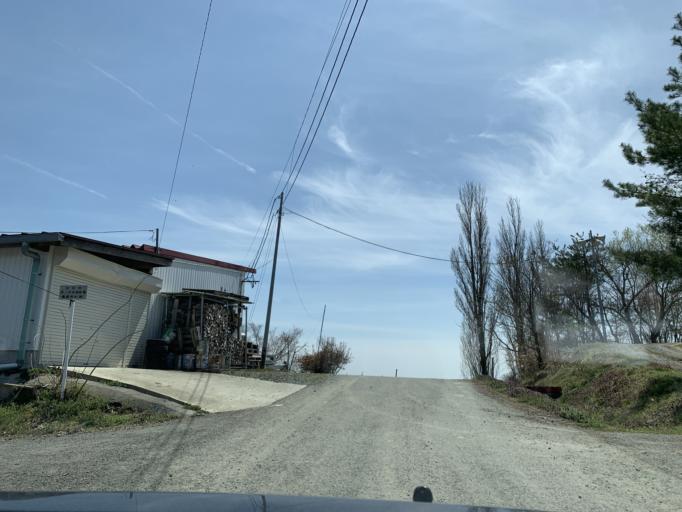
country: JP
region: Iwate
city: Ichinoseki
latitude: 38.8100
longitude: 141.2721
